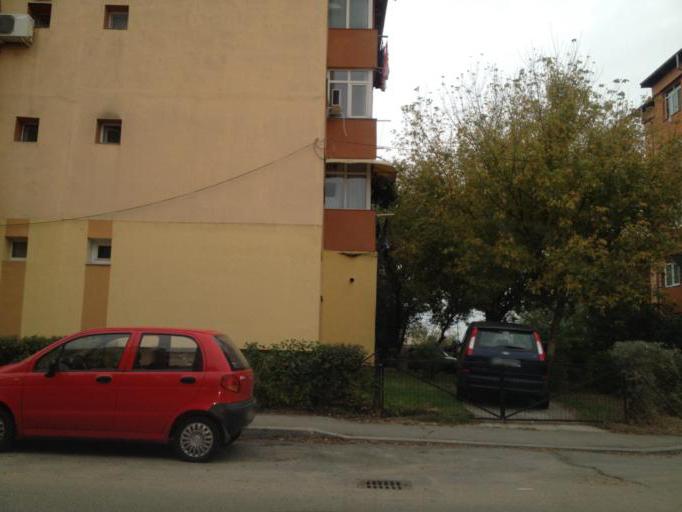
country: RO
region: Dolj
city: Craiova
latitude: 44.3322
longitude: 23.7906
